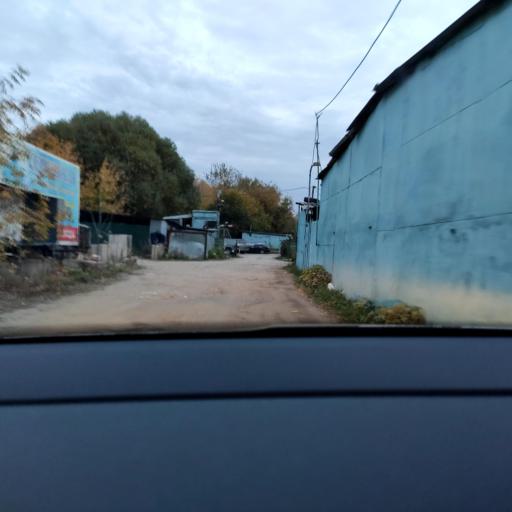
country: RU
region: Moscow
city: Bibirevo
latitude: 55.8833
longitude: 37.6132
